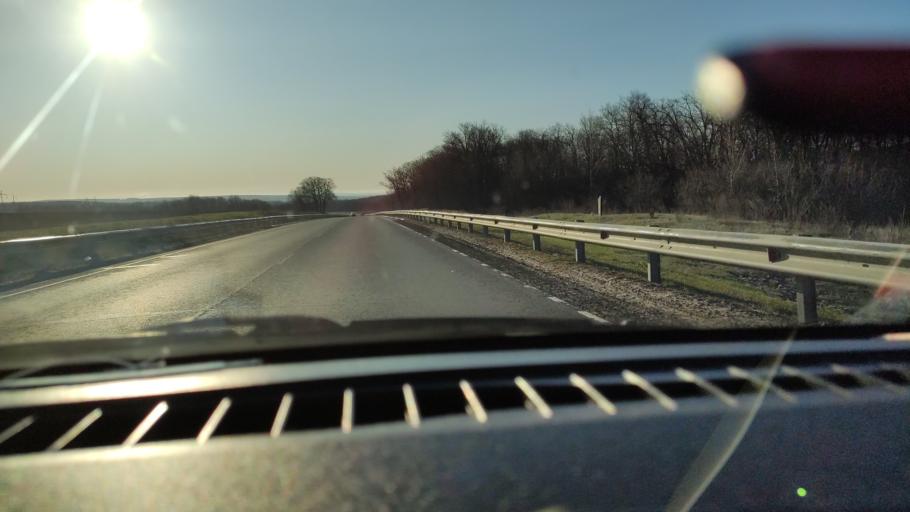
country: RU
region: Saratov
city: Vol'sk
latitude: 52.1035
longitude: 47.4484
